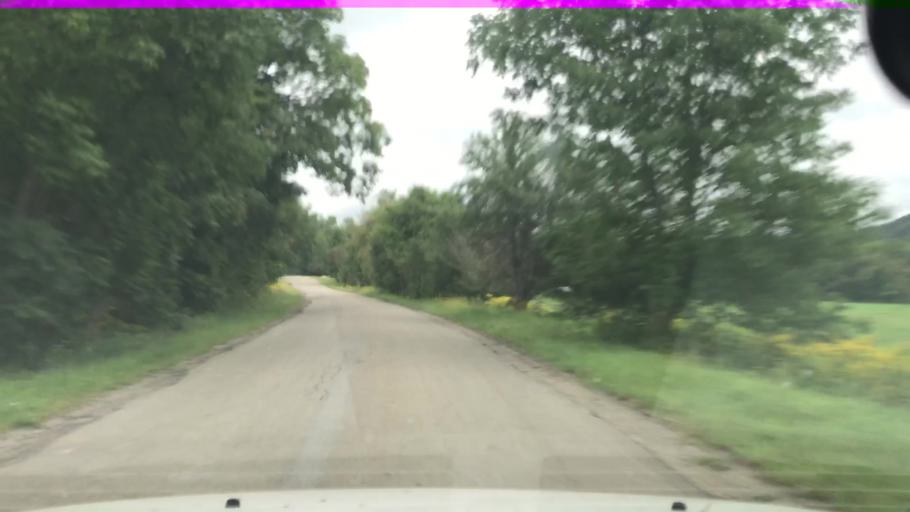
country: US
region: New York
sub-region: Cattaraugus County
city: Little Valley
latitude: 42.3150
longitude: -78.7216
